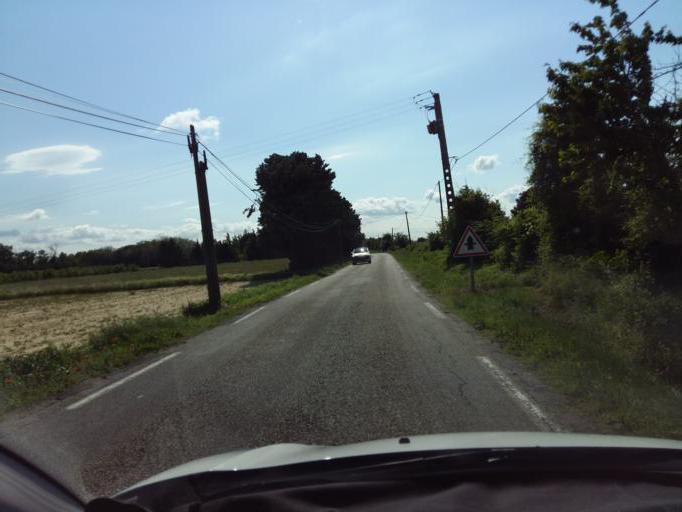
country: FR
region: Provence-Alpes-Cote d'Azur
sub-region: Departement du Vaucluse
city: Robion
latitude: 43.8629
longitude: 5.1052
